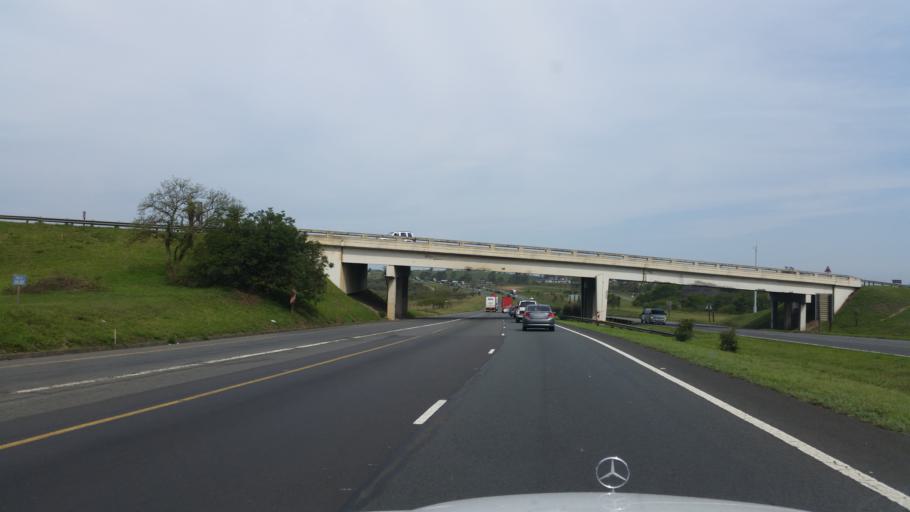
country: ZA
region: KwaZulu-Natal
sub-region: uMgungundlovu District Municipality
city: Camperdown
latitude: -29.7188
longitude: 30.4977
